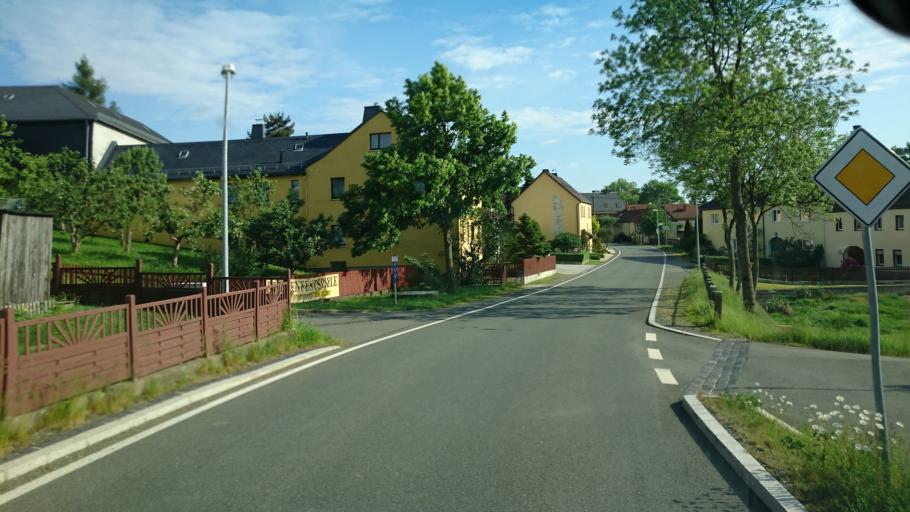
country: DE
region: Saxony
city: Reuth
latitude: 50.4887
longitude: 11.9453
